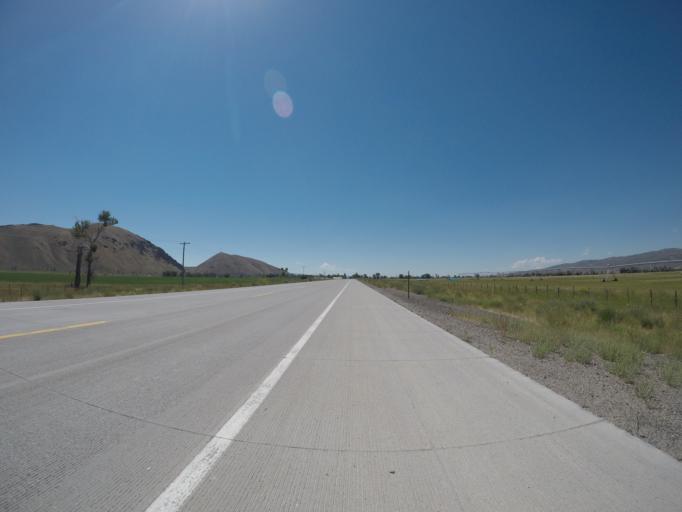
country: US
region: Idaho
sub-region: Bear Lake County
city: Montpelier
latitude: 42.1064
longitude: -110.9547
